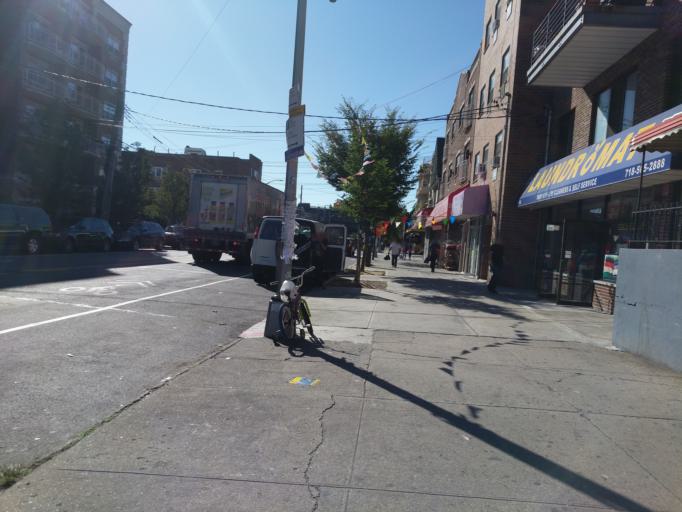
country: US
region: New York
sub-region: Queens County
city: Borough of Queens
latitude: 40.7520
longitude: -73.8595
